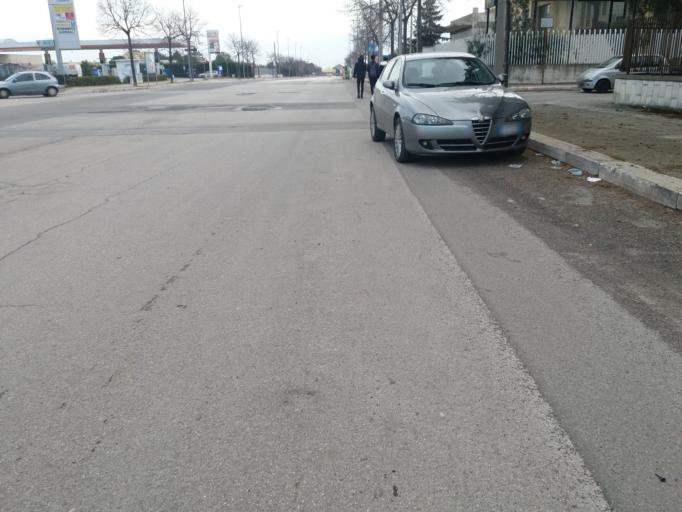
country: IT
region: Apulia
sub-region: Provincia di Bari
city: Bitonto
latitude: 41.1153
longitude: 16.6849
